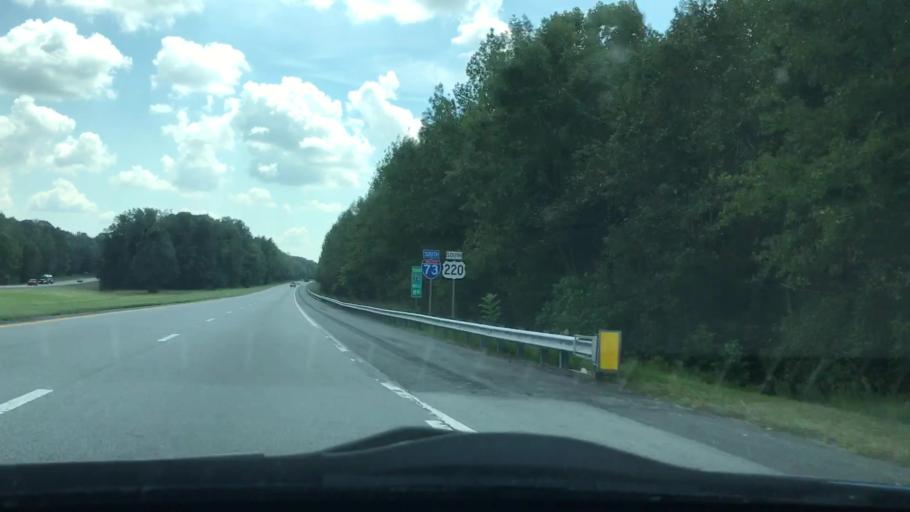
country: US
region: North Carolina
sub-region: Guilford County
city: Pleasant Garden
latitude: 35.9162
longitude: -79.8241
